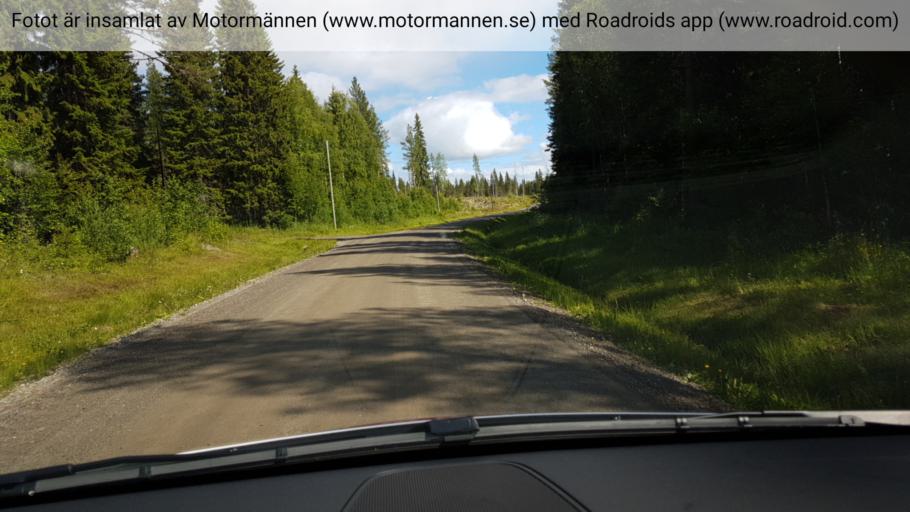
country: SE
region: Vaesterbotten
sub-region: Dorotea Kommun
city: Dorotea
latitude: 64.0955
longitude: 16.4918
